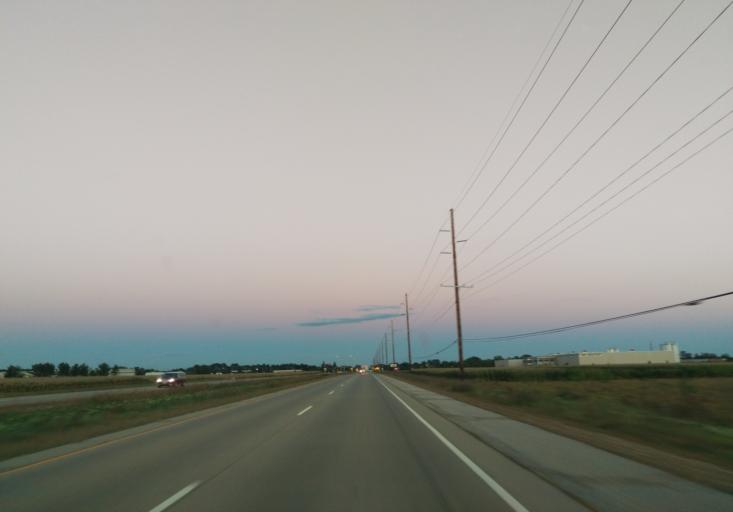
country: US
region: Wisconsin
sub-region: Rock County
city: Janesville
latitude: 42.7269
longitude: -89.0210
